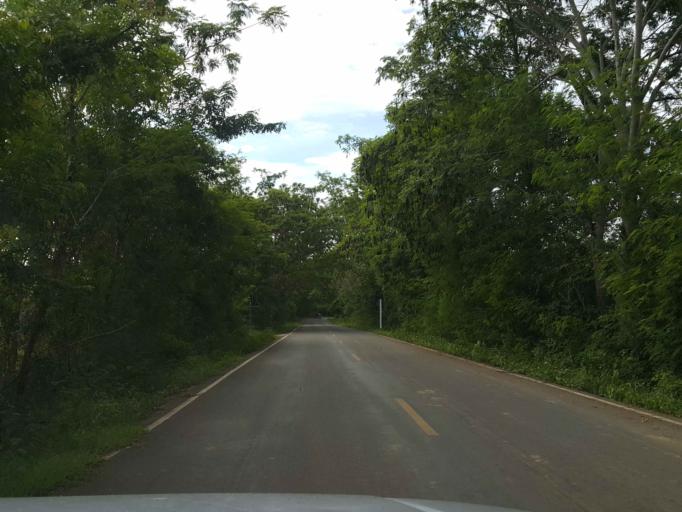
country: TH
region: Sukhothai
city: Thung Saliam
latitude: 17.3119
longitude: 99.5235
